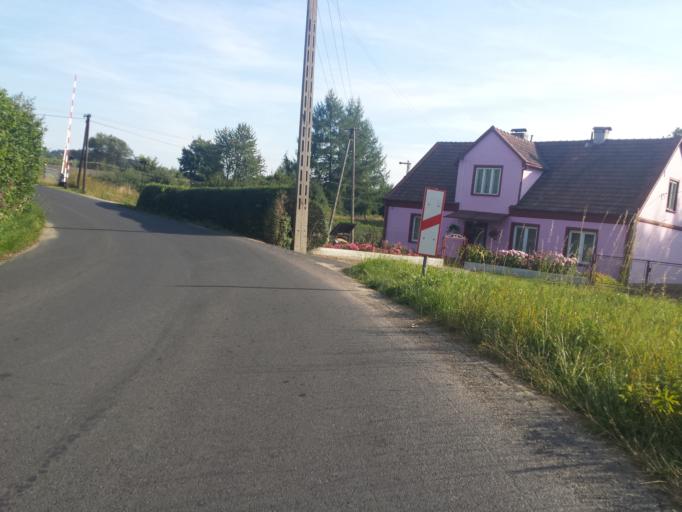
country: PL
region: Subcarpathian Voivodeship
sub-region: Powiat leski
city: Uherce Mineralne
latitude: 49.4638
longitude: 22.3970
